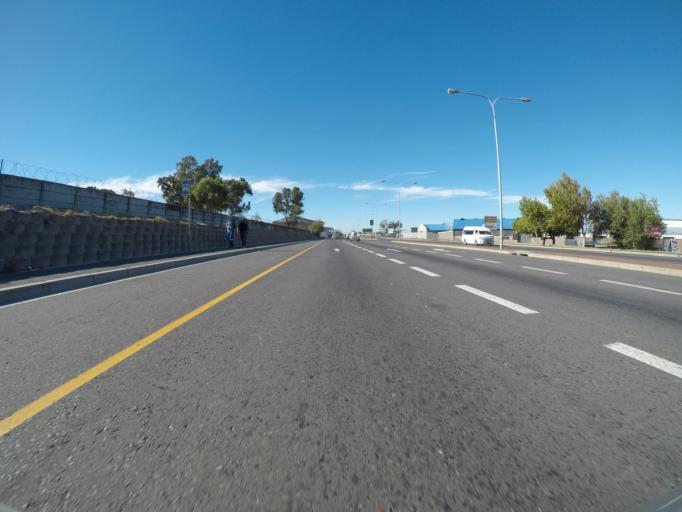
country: ZA
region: Western Cape
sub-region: City of Cape Town
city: Kraaifontein
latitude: -33.9082
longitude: 18.6664
